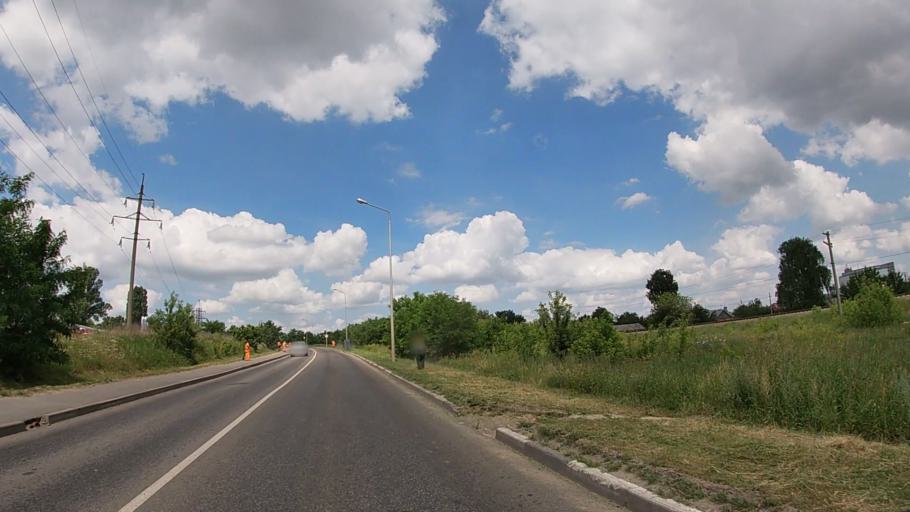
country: RU
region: Belgorod
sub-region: Belgorodskiy Rayon
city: Belgorod
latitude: 50.5930
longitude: 36.5605
